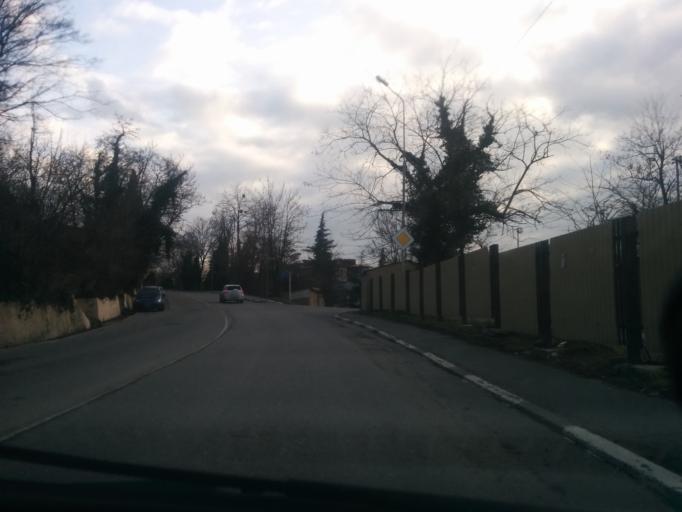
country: RU
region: Krasnodarskiy
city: Tuapse
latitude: 44.1101
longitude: 39.0624
